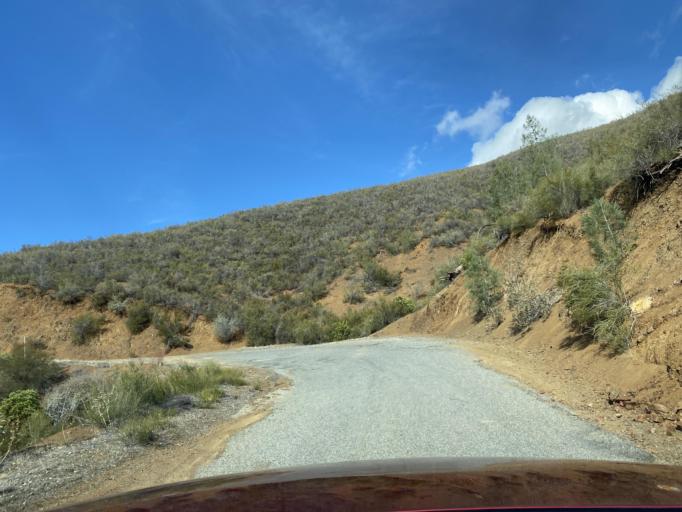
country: US
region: California
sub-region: Lake County
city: Lucerne
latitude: 39.3649
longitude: -122.6301
